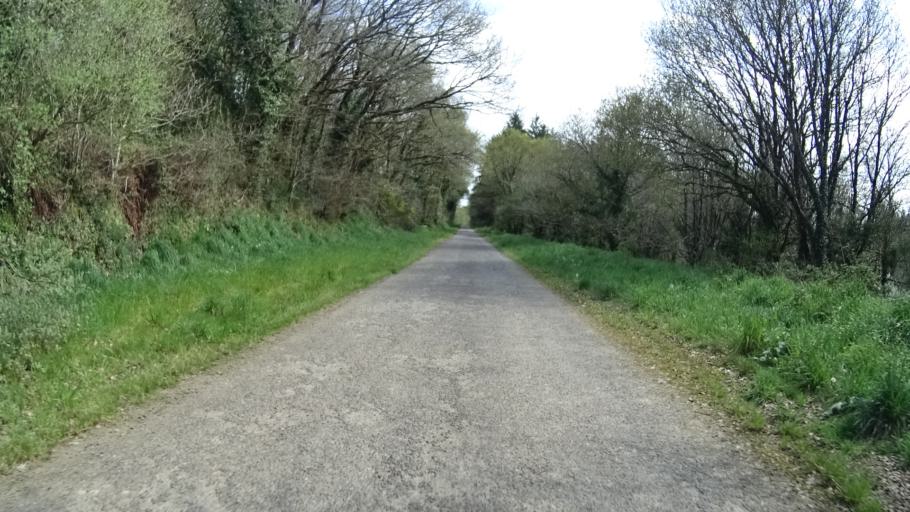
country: FR
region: Brittany
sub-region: Departement du Finistere
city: Sizun
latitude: 48.4247
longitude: -4.1018
